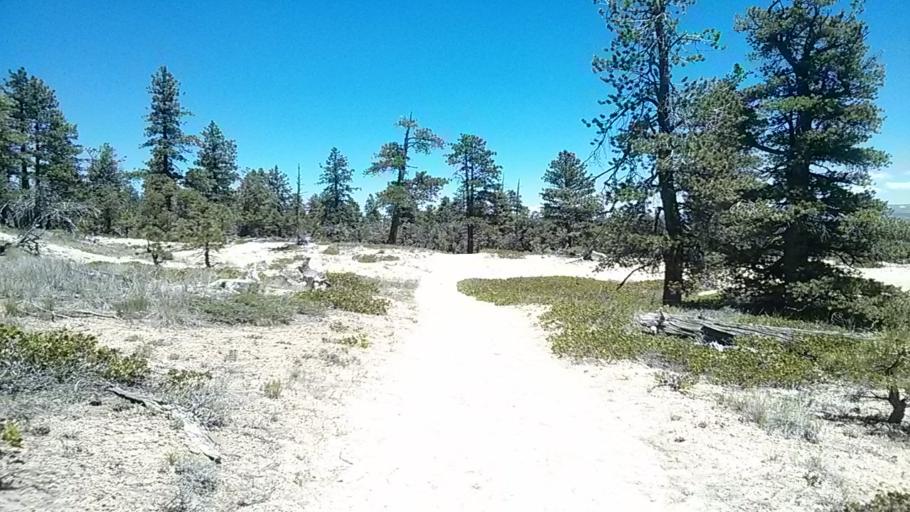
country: US
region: Utah
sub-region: Garfield County
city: Panguitch
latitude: 37.6431
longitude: -112.1553
